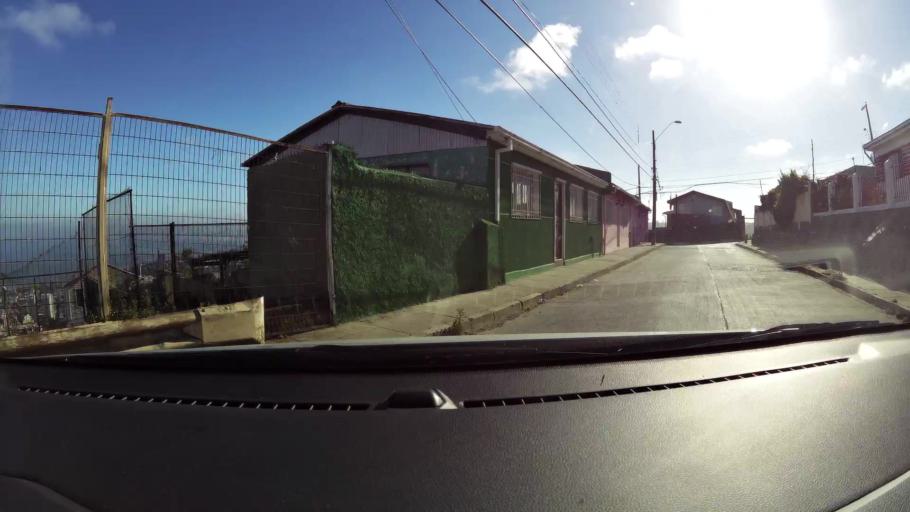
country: CL
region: Valparaiso
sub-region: Provincia de Valparaiso
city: Valparaiso
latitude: -33.0609
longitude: -71.6089
